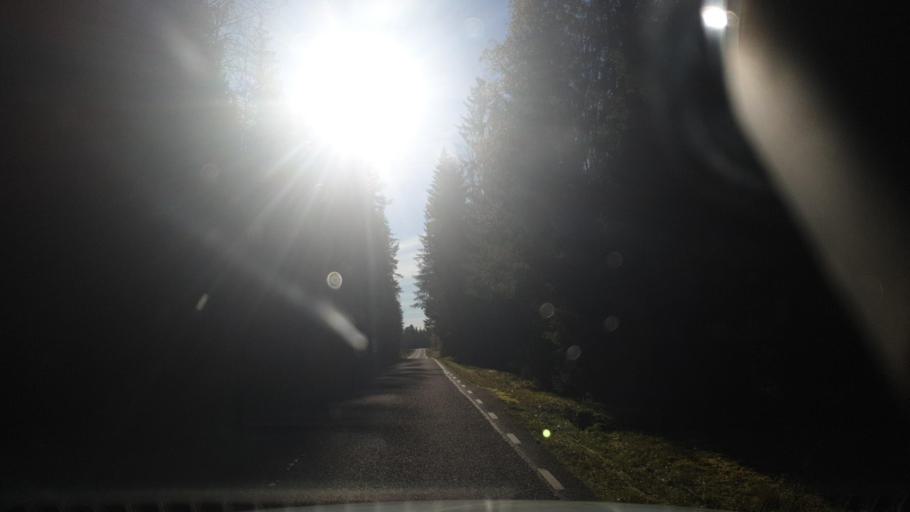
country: SE
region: Vaermland
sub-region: Karlstads Kommun
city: Edsvalla
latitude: 59.5278
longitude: 13.1114
